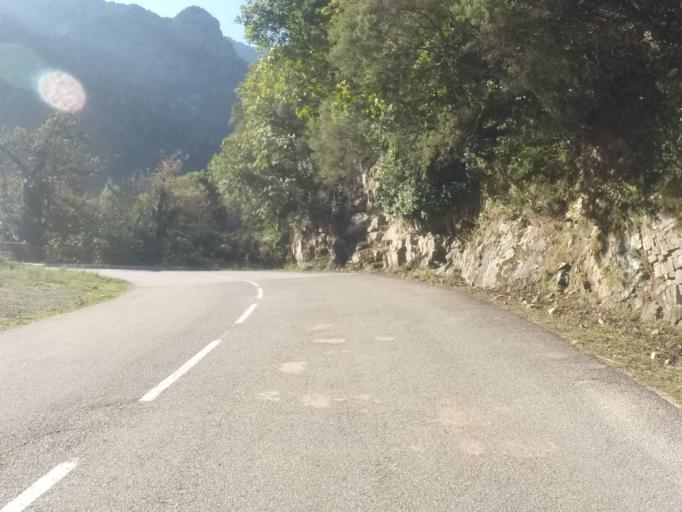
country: FR
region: Corsica
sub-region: Departement de la Corse-du-Sud
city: Cargese
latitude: 42.2417
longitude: 8.7320
